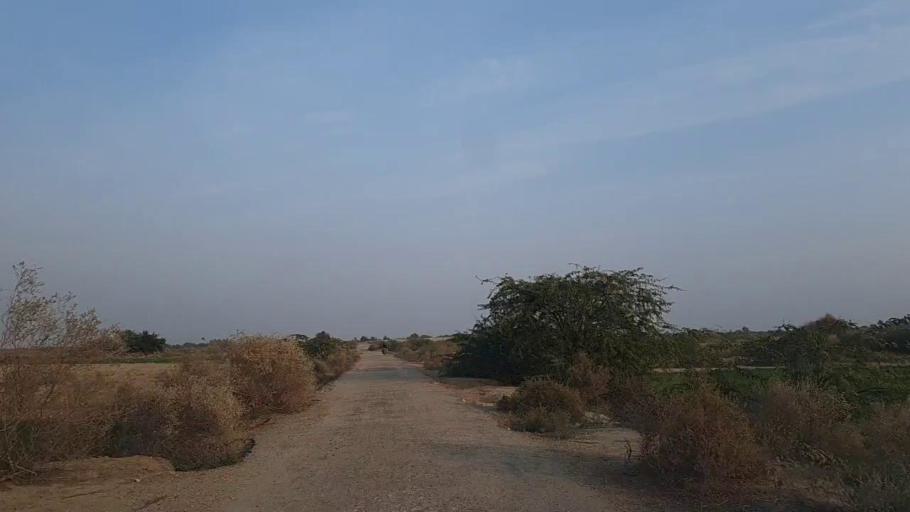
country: PK
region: Sindh
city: Jam Sahib
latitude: 26.4076
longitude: 68.5935
